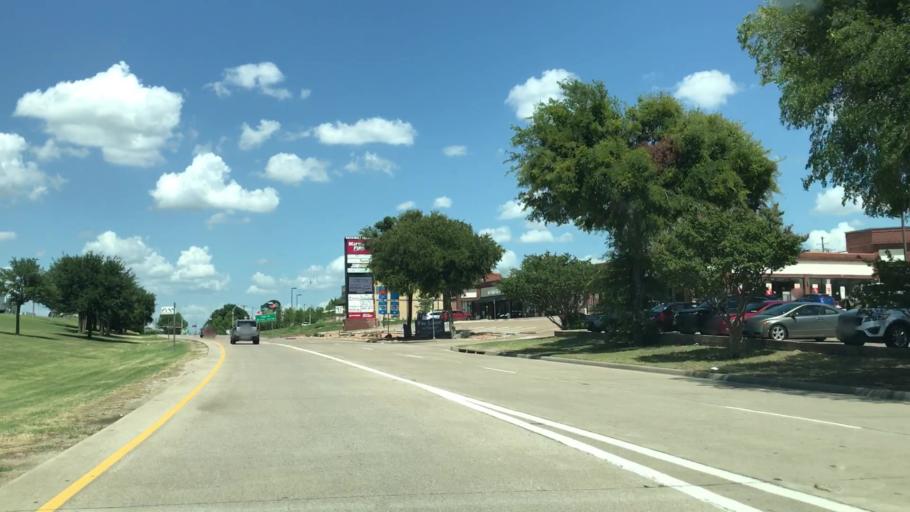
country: US
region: Texas
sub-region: Rockwall County
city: Rockwall
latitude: 32.8959
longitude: -96.4728
